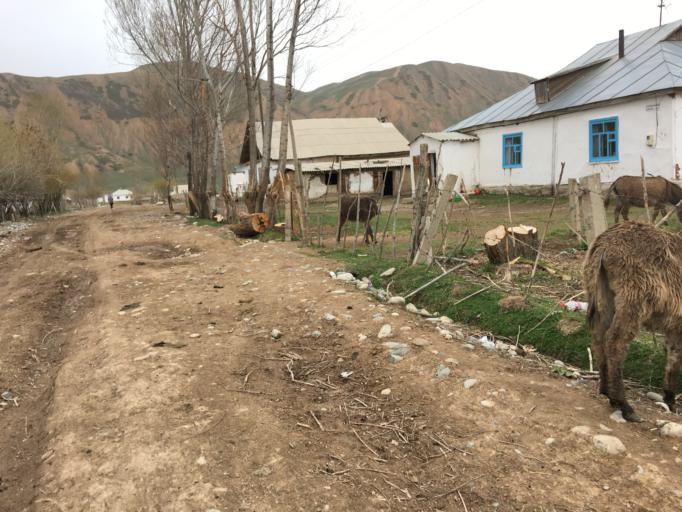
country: KG
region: Naryn
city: Naryn
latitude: 41.5194
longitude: 76.4388
